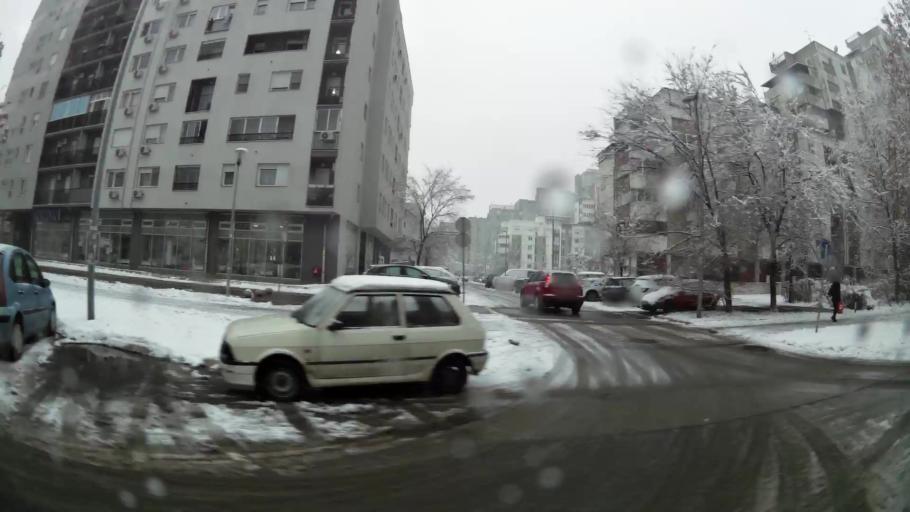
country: RS
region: Central Serbia
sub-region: Belgrade
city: Cukarica
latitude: 44.8008
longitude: 20.3756
